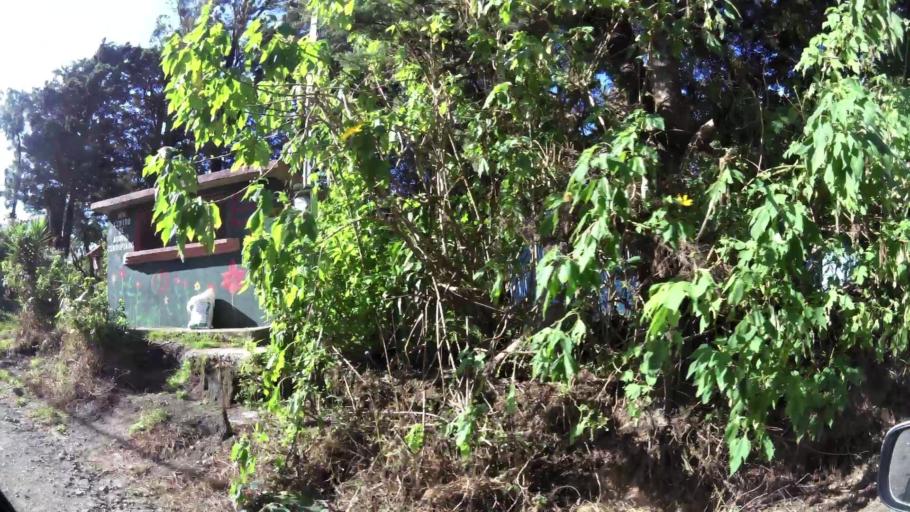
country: CR
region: Guanacaste
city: Juntas
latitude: 10.3141
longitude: -84.8174
